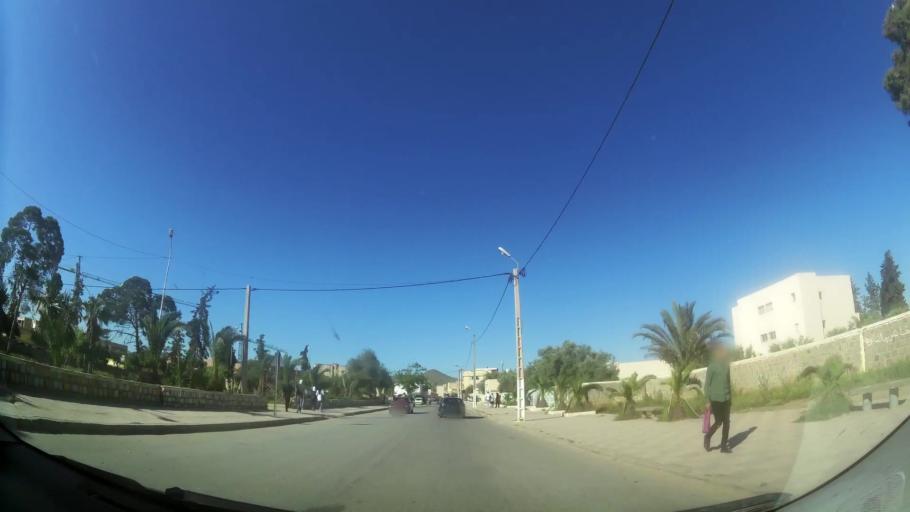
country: MA
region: Oriental
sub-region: Berkane-Taourirt
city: Ahfir
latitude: 34.9488
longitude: -2.1029
